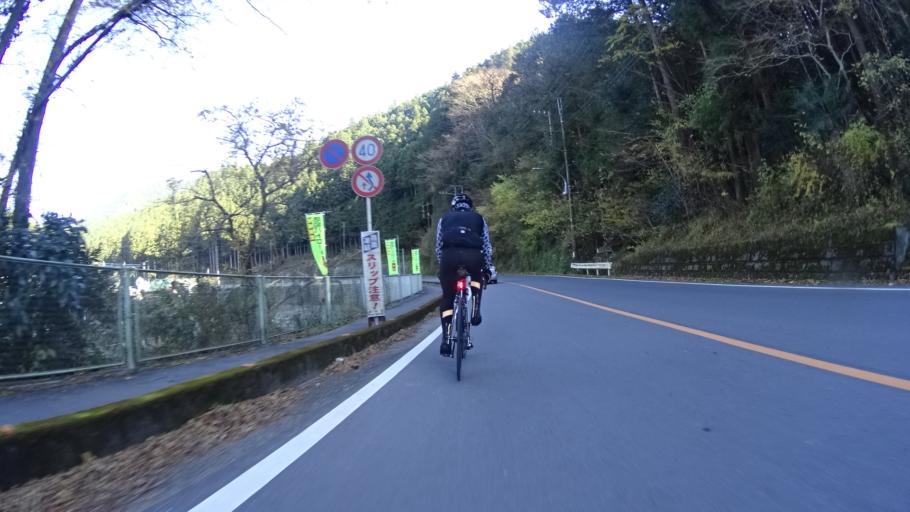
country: JP
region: Tokyo
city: Ome
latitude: 35.8722
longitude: 139.1868
